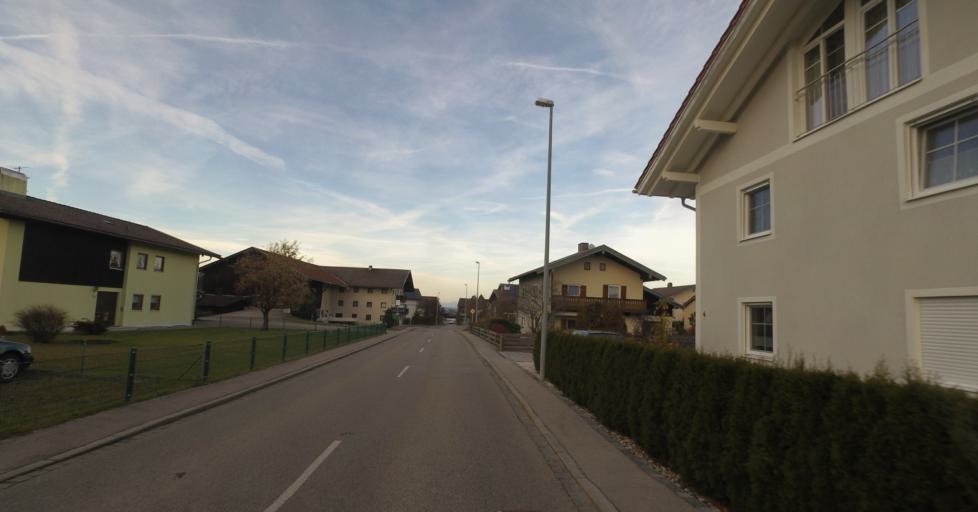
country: DE
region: Bavaria
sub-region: Upper Bavaria
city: Vachendorf
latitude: 47.8787
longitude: 12.6096
